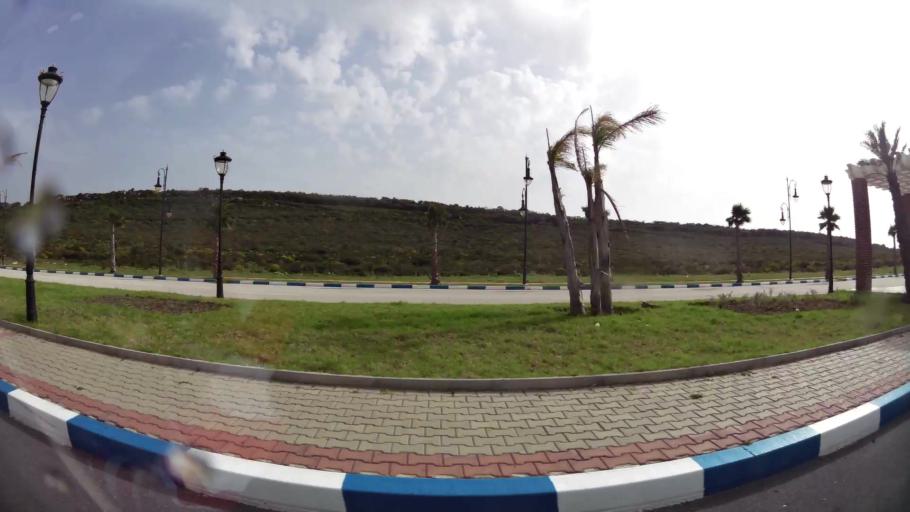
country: MA
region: Tanger-Tetouan
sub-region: Tanger-Assilah
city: Boukhalef
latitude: 35.6975
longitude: -5.9267
